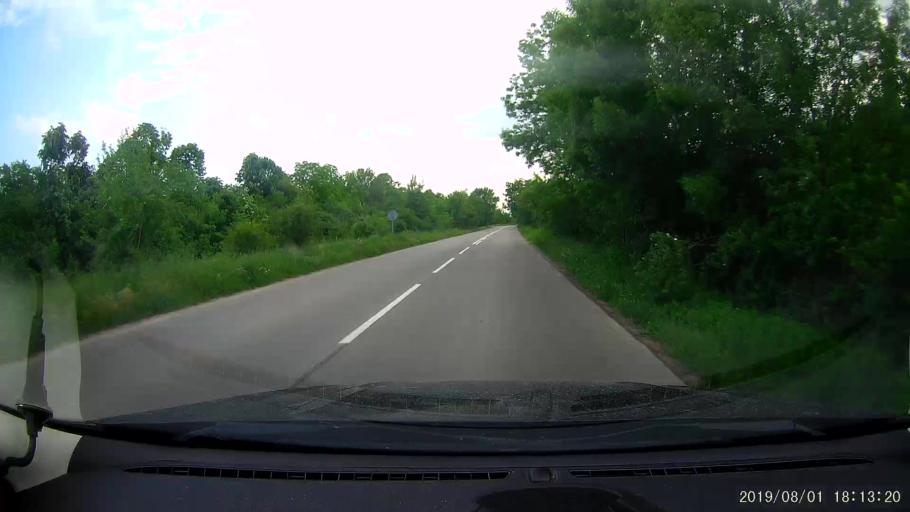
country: BG
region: Silistra
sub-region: Obshtina Dulovo
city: Dulovo
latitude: 43.7911
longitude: 27.1413
